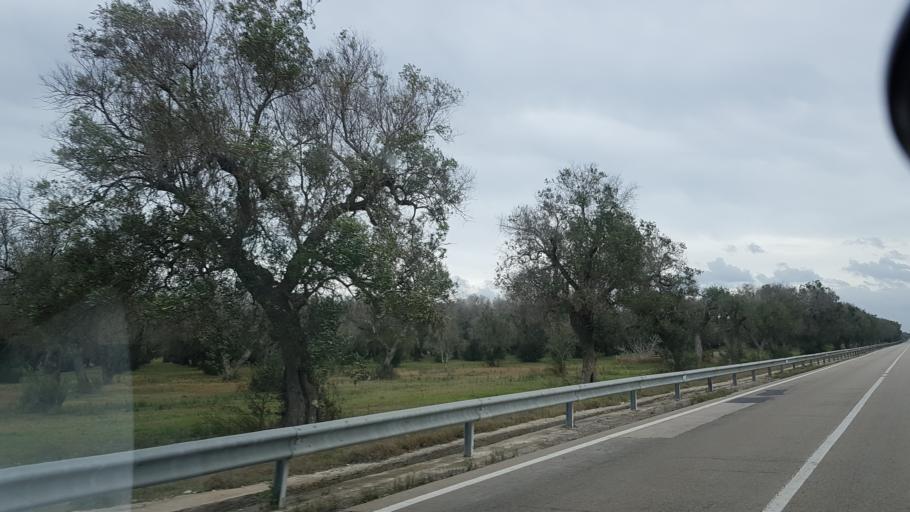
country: IT
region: Apulia
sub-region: Provincia di Brindisi
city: San Pancrazio Salentino
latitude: 40.4071
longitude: 17.8856
